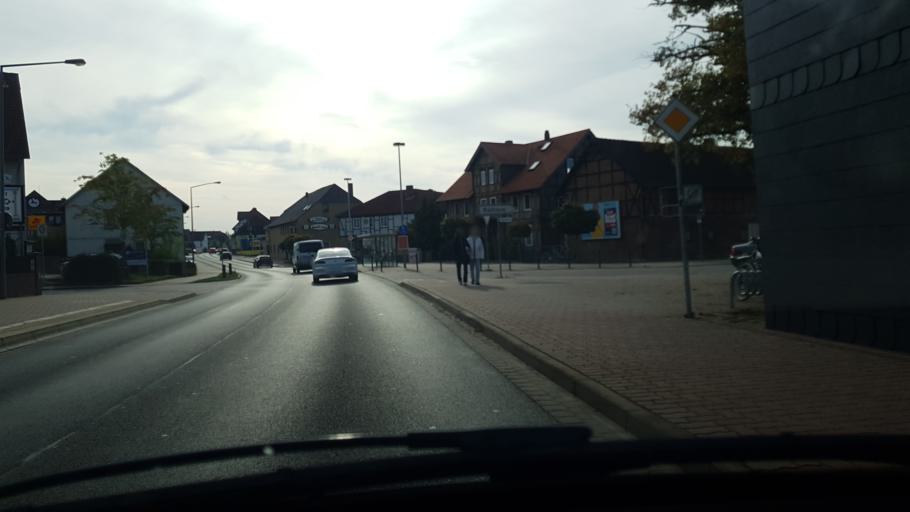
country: DE
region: Lower Saxony
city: Lehre
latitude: 52.3293
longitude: 10.6686
